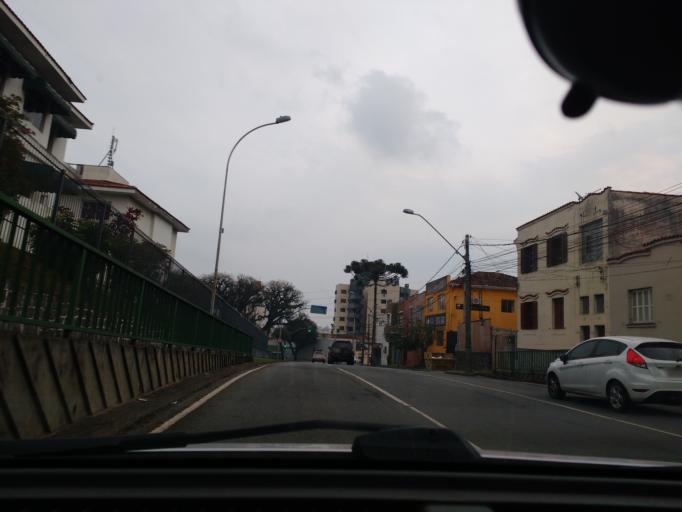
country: BR
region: Parana
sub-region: Curitiba
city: Curitiba
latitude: -25.4237
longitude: -49.2812
